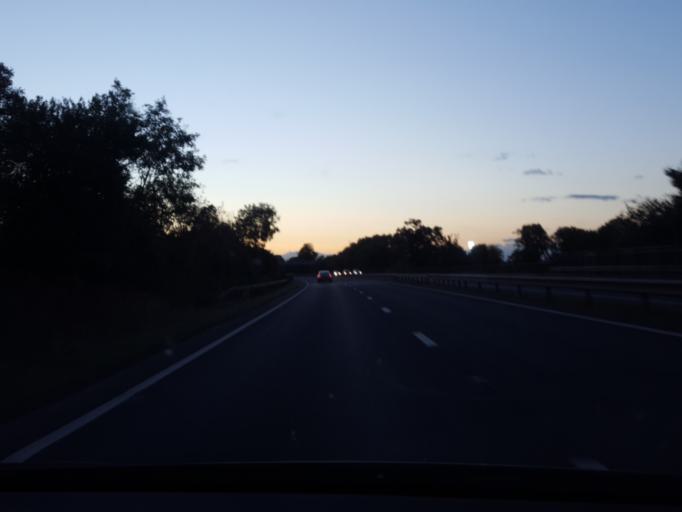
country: GB
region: England
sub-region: Leicestershire
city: Barrow upon Soar
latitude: 52.7471
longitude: -1.1563
